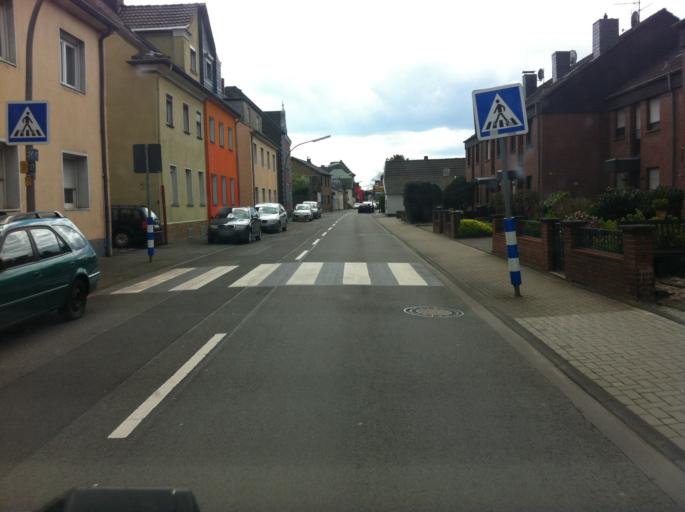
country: DE
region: North Rhine-Westphalia
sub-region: Regierungsbezirk Koln
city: Sinnersdorf
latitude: 51.0491
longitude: 6.8483
